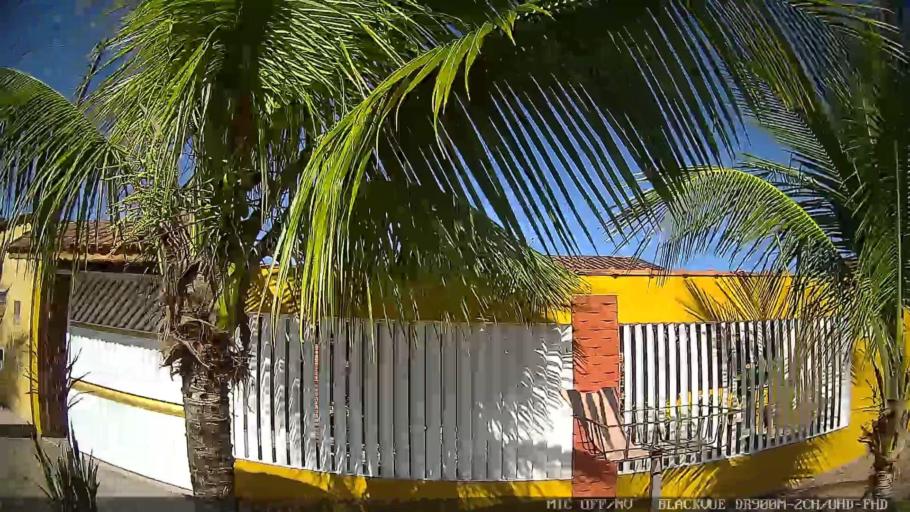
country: BR
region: Sao Paulo
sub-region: Itanhaem
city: Itanhaem
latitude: -24.2217
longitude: -46.8706
